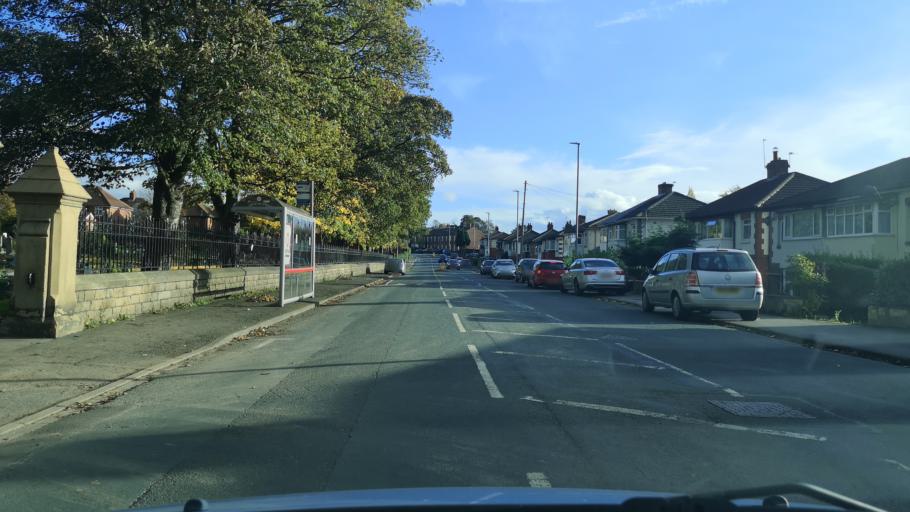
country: GB
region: England
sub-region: Kirklees
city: Dewsbury
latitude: 53.6843
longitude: -1.6537
